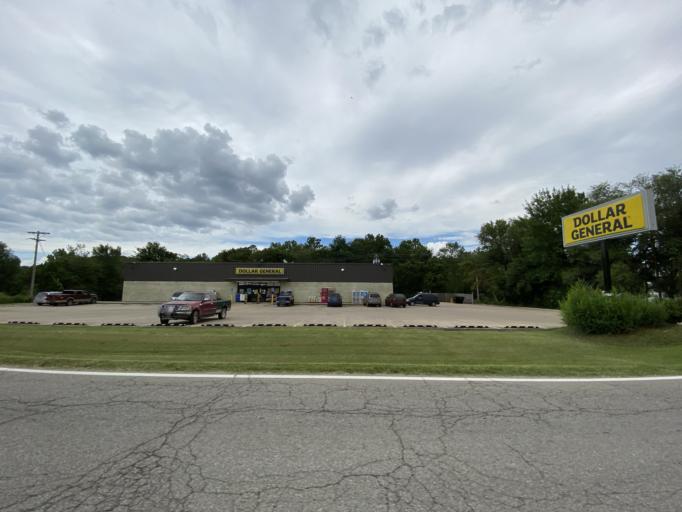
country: US
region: Arkansas
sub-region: Fulton County
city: Salem
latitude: 36.3691
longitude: -91.8227
